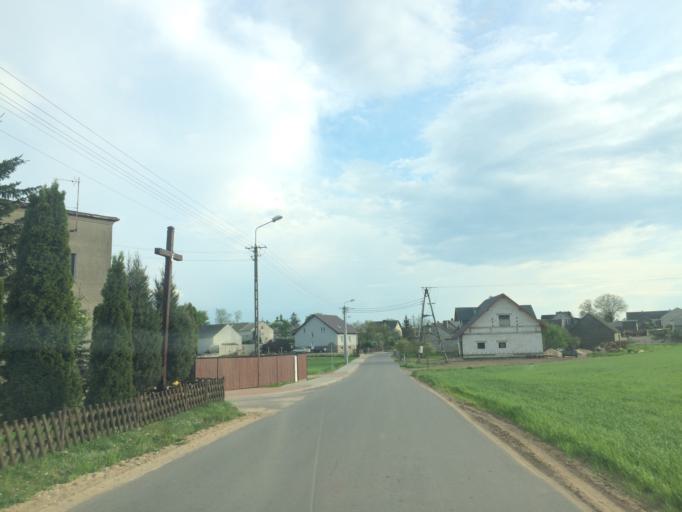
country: PL
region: Kujawsko-Pomorskie
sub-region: Powiat brodnicki
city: Brzozie
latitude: 53.3596
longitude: 19.7101
